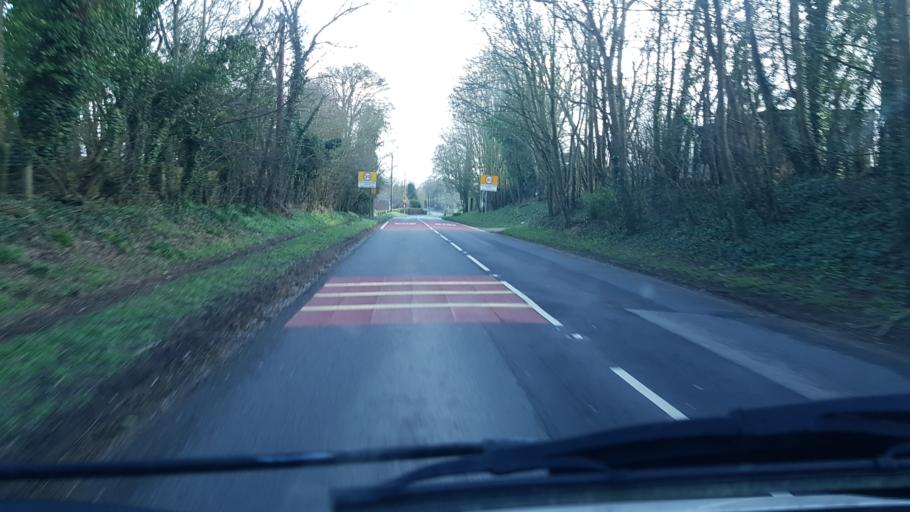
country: GB
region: England
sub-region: Wiltshire
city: Collingbourne Kingston
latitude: 51.2916
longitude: -1.6540
